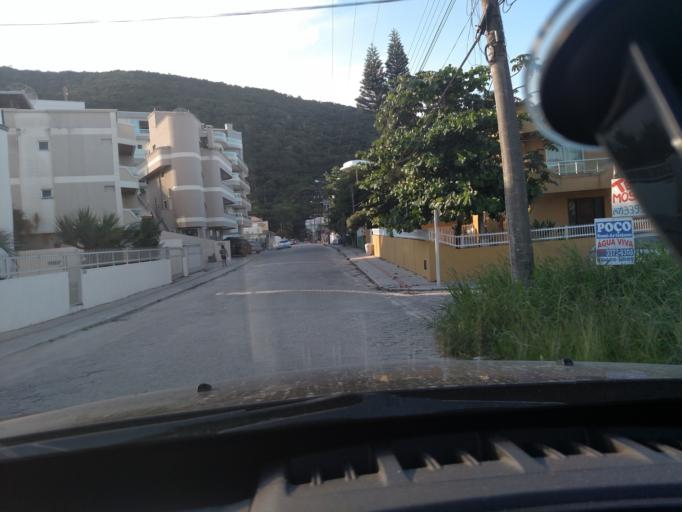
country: BR
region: Santa Catarina
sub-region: Porto Belo
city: Porto Belo
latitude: -27.1344
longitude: -48.5138
